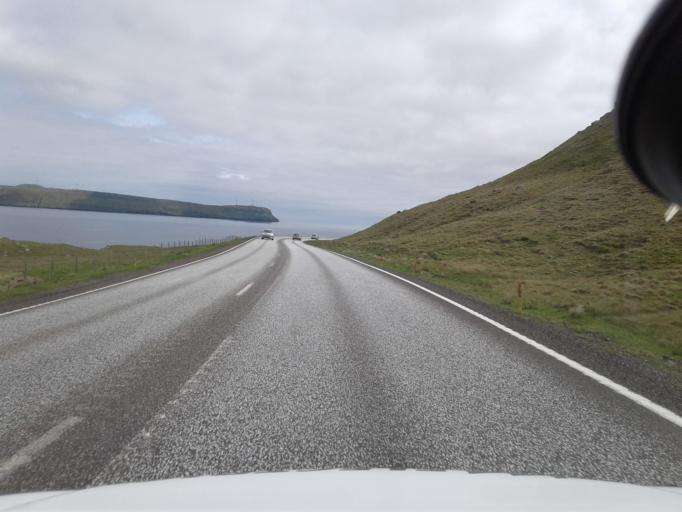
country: FO
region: Streymoy
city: Hoyvik
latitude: 62.0504
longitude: -6.7993
